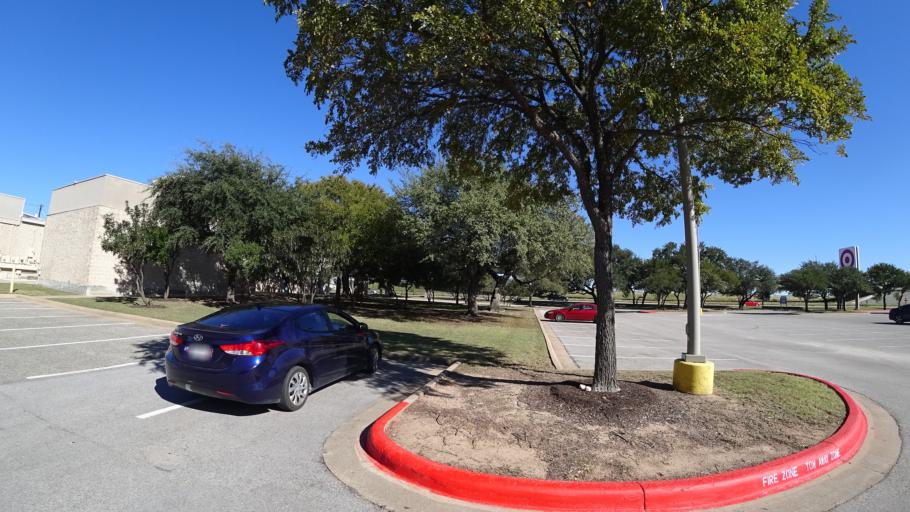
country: US
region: Texas
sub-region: Travis County
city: Rollingwood
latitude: 30.2346
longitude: -97.8270
